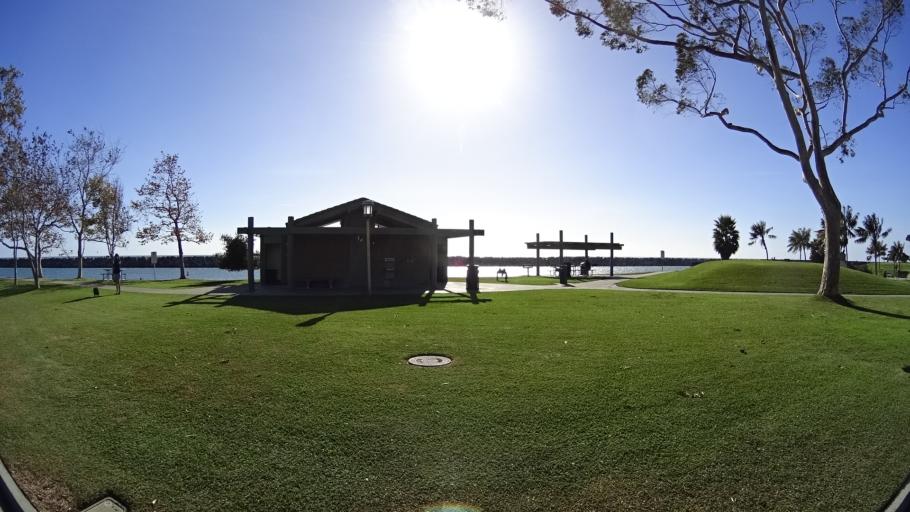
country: US
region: California
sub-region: Orange County
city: Dana Point
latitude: 33.4584
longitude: -117.6993
